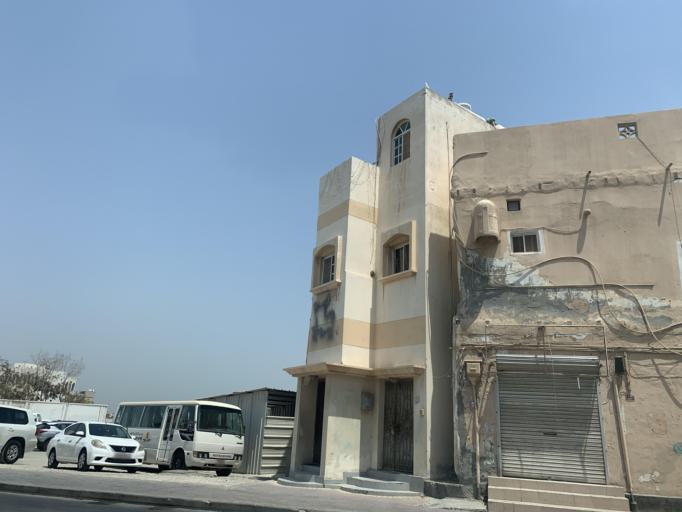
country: BH
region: Manama
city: Jidd Hafs
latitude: 26.2055
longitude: 50.5532
